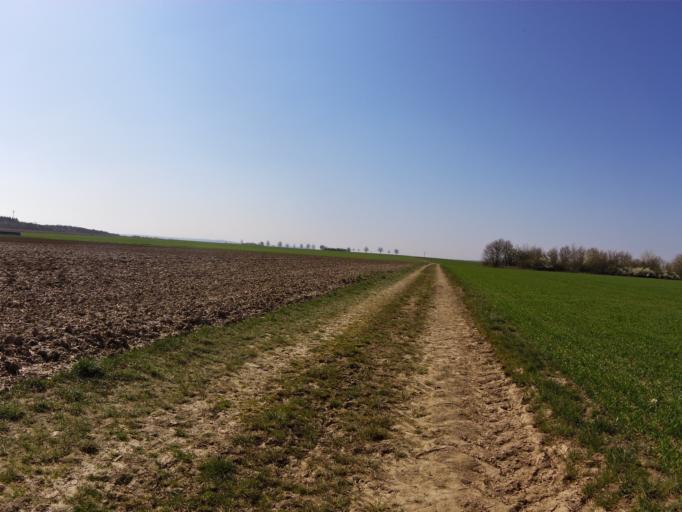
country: DE
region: Bavaria
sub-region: Regierungsbezirk Unterfranken
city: Kurnach
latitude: 49.8375
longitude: 10.0513
